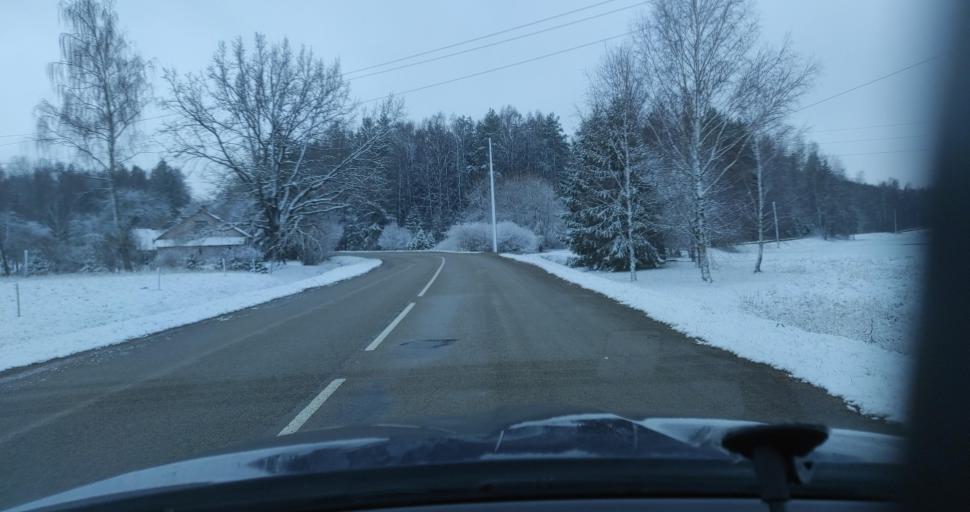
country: LV
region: Skrunda
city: Skrunda
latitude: 56.8673
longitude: 22.2324
